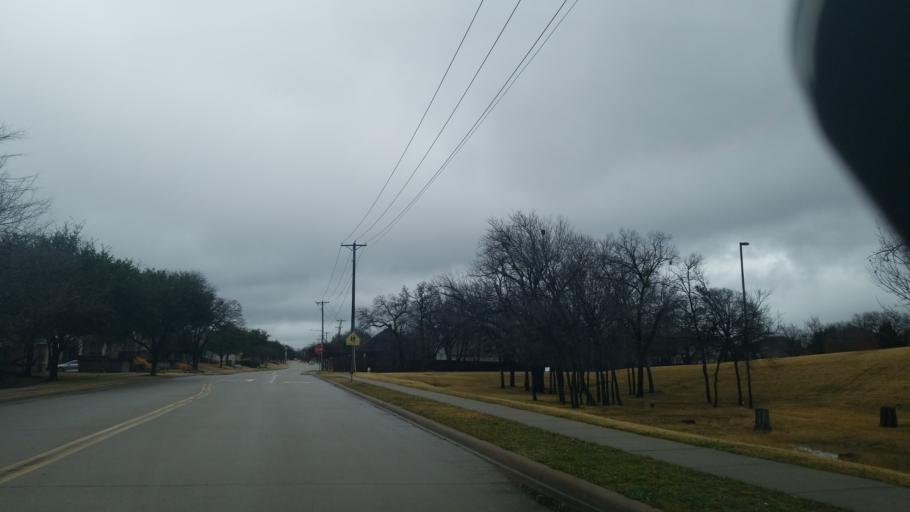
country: US
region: Texas
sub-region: Denton County
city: Corinth
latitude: 33.1478
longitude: -97.0853
